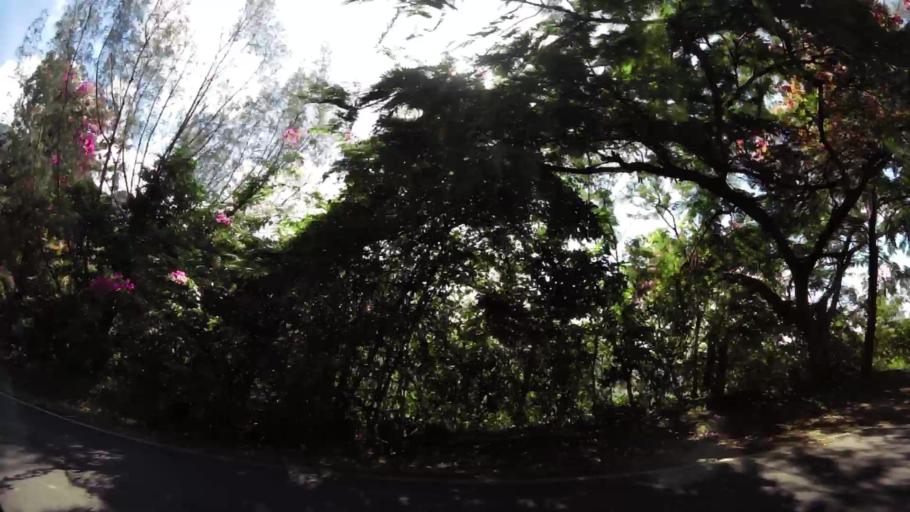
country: LC
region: Soufriere
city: Soufriere
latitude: 13.8637
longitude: -61.0542
